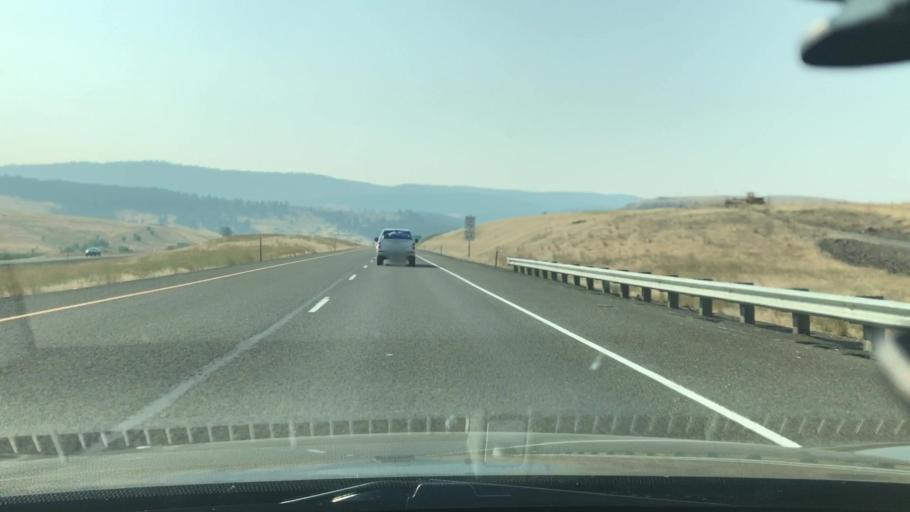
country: US
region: Oregon
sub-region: Union County
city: Union
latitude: 45.1893
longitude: -117.9947
